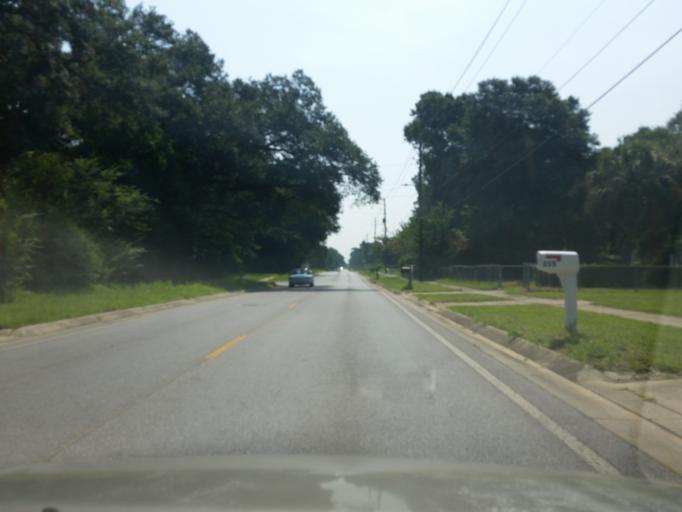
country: US
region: Florida
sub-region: Escambia County
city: Ensley
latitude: 30.5193
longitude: -87.2616
